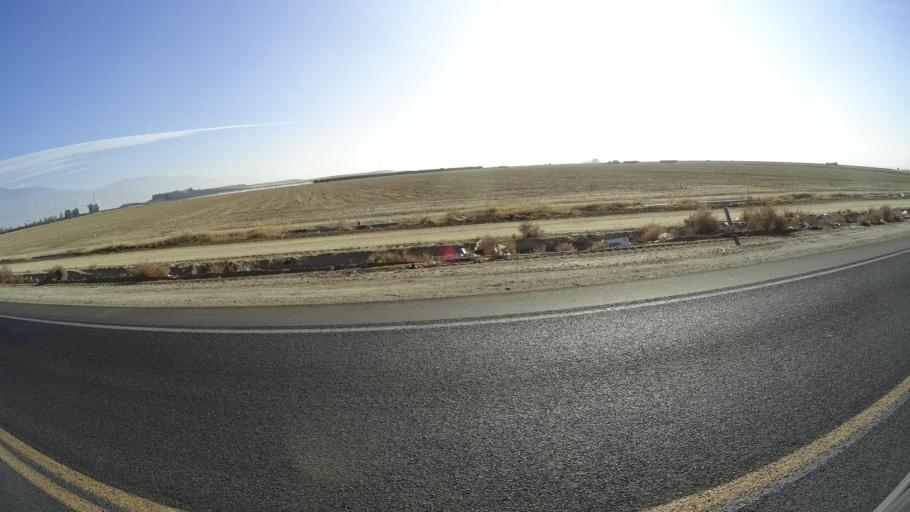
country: US
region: California
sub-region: Kern County
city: Arvin
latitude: 35.3301
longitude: -118.7966
